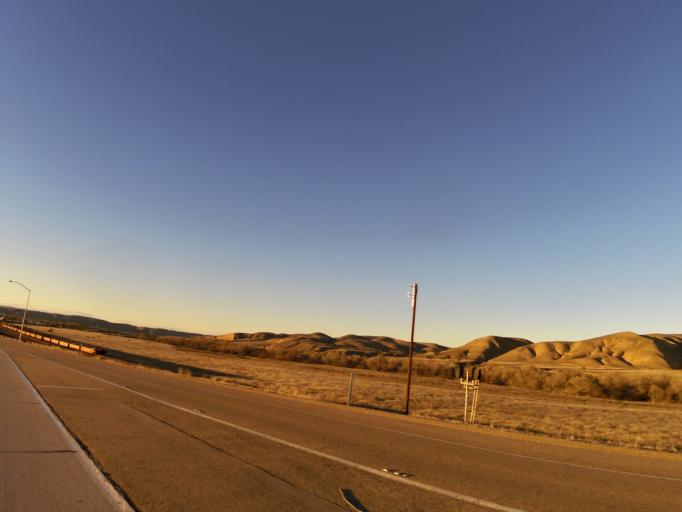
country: US
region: California
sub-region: San Luis Obispo County
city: San Miguel
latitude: 35.7775
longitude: -120.7157
